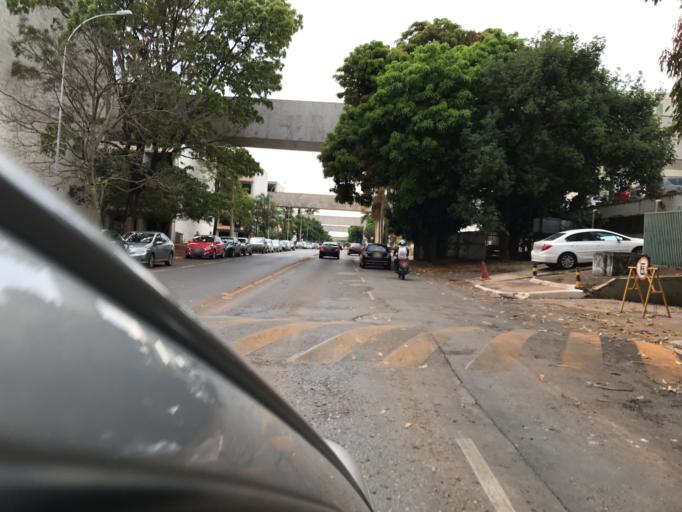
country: BR
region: Federal District
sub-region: Brasilia
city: Brasilia
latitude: -15.7941
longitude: -47.8723
